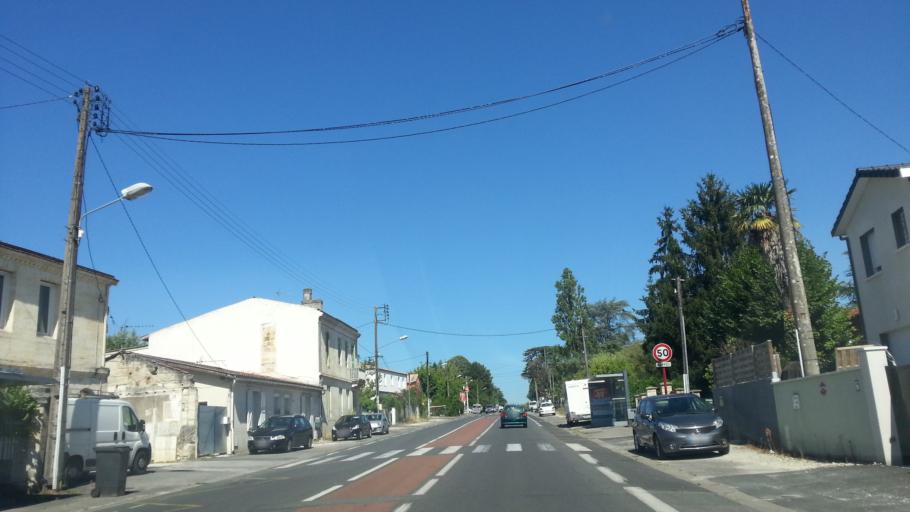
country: FR
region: Aquitaine
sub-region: Departement de la Gironde
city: Villenave-d'Ornon
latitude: 44.7599
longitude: -0.5561
